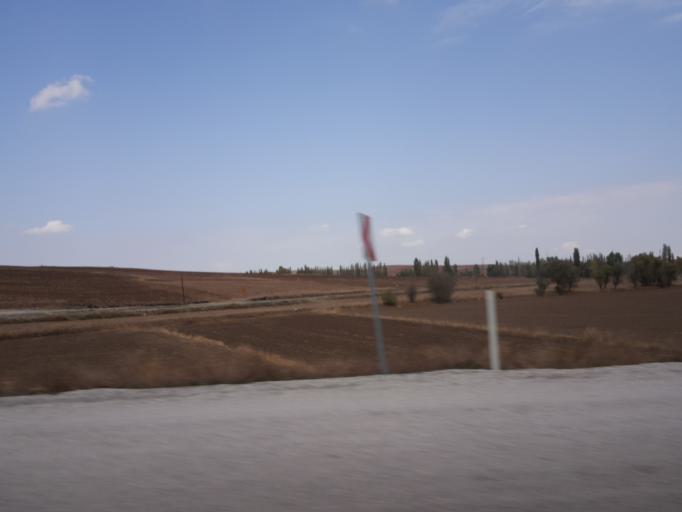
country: TR
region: Corum
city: Alaca
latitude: 40.1555
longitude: 34.7564
